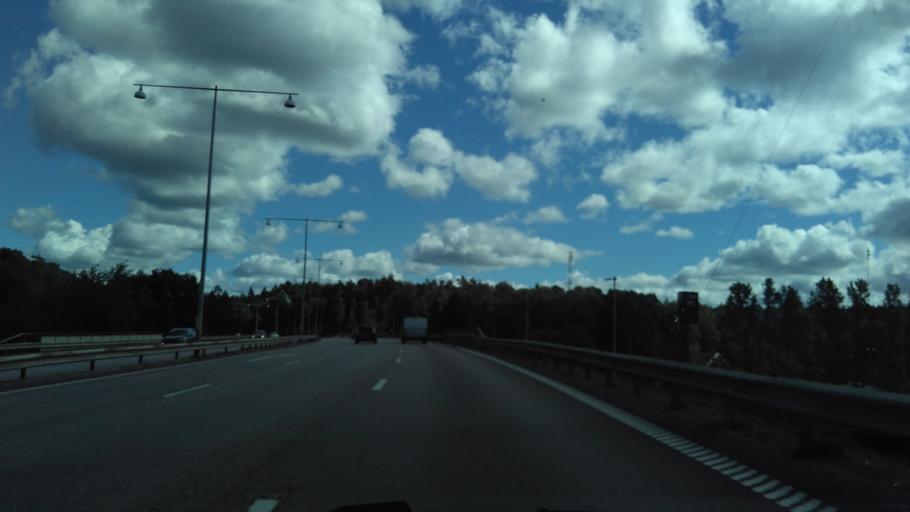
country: SE
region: Vaestra Goetaland
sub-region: Molndal
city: Moelndal
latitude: 57.6770
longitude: 12.0251
